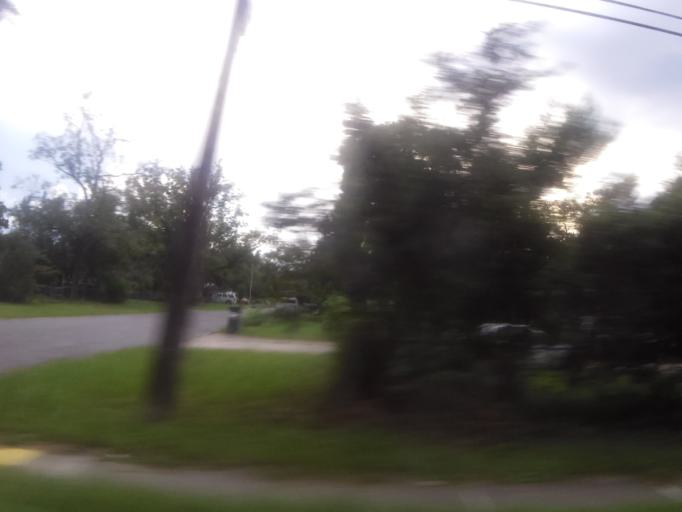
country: US
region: Florida
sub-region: Clay County
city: Bellair-Meadowbrook Terrace
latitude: 30.2844
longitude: -81.7783
